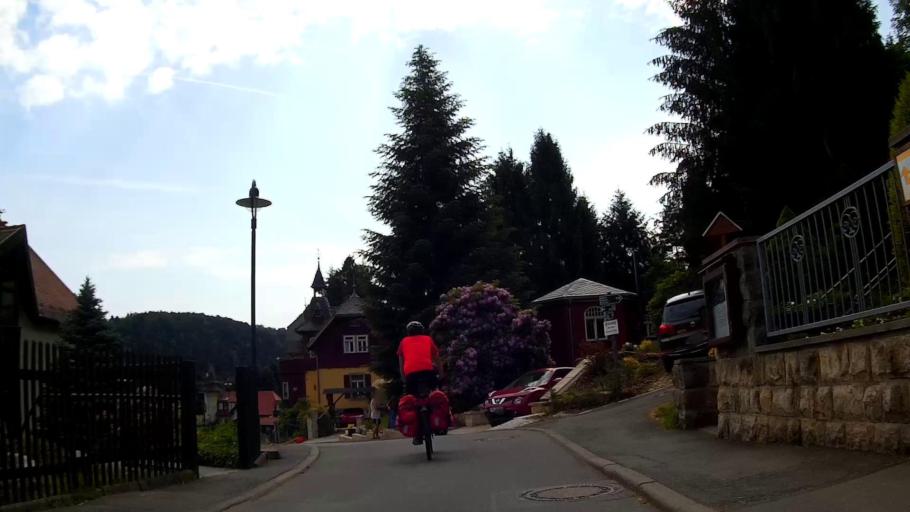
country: DE
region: Saxony
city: Konigstein
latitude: 50.9563
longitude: 14.0744
